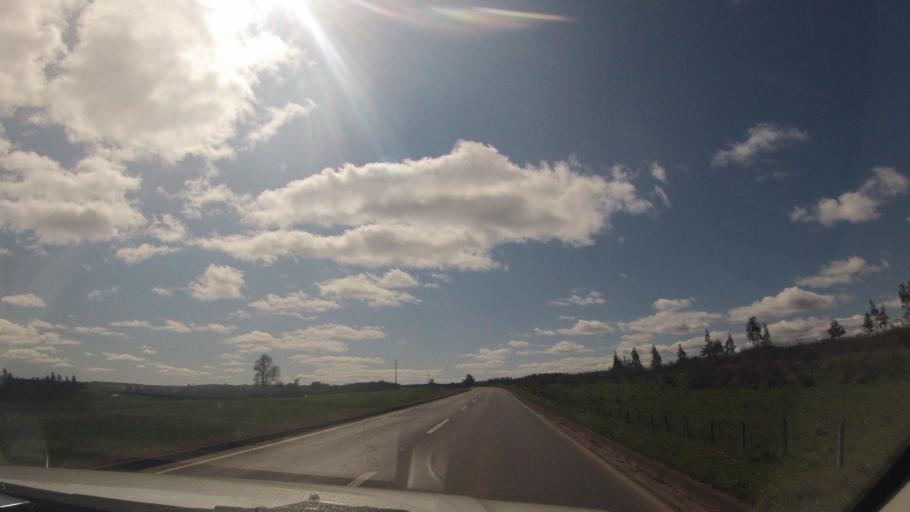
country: CL
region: Araucania
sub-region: Provincia de Malleco
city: Traiguen
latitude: -38.2275
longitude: -72.7089
